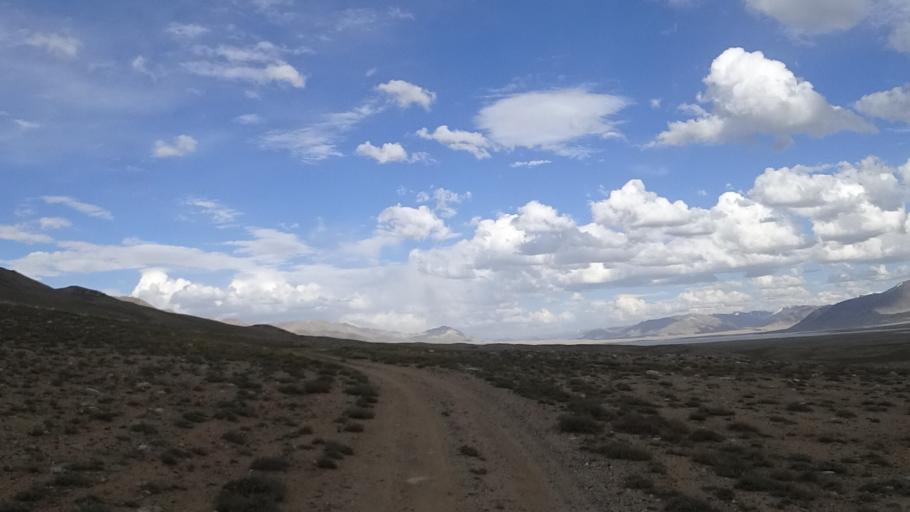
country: TJ
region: Gorno-Badakhshan
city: Murghob
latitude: 37.4685
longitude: 73.5870
